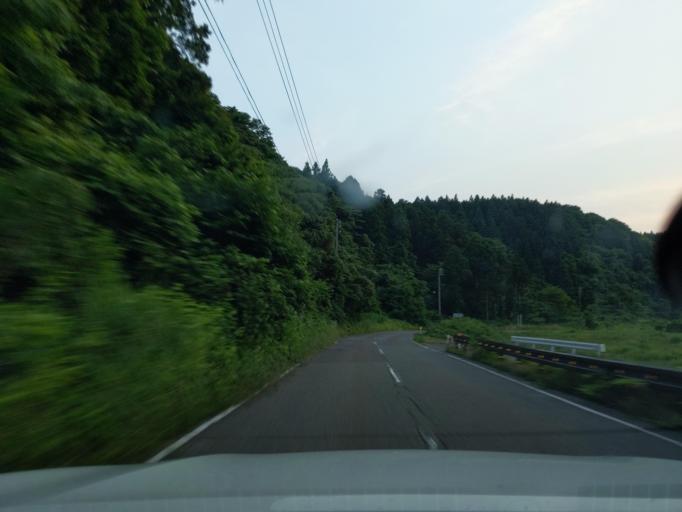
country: JP
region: Niigata
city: Kashiwazaki
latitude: 37.4520
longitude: 138.6261
